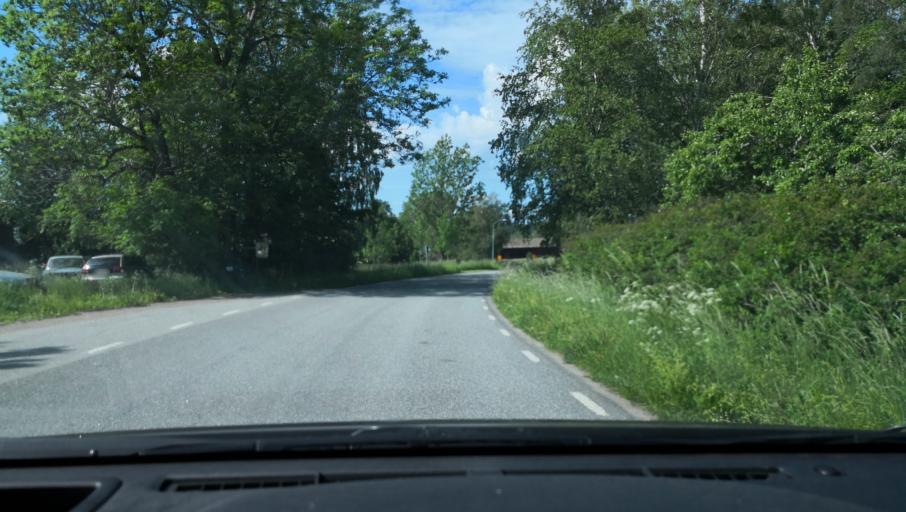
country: SE
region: Uppsala
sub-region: Enkopings Kommun
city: Orsundsbro
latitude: 59.8268
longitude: 17.3188
